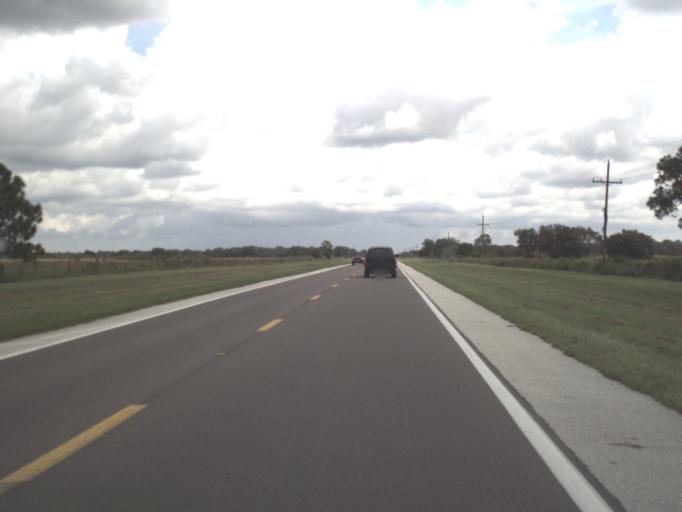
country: US
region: Florida
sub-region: Hendry County
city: LaBelle
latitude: 26.7917
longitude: -81.4307
